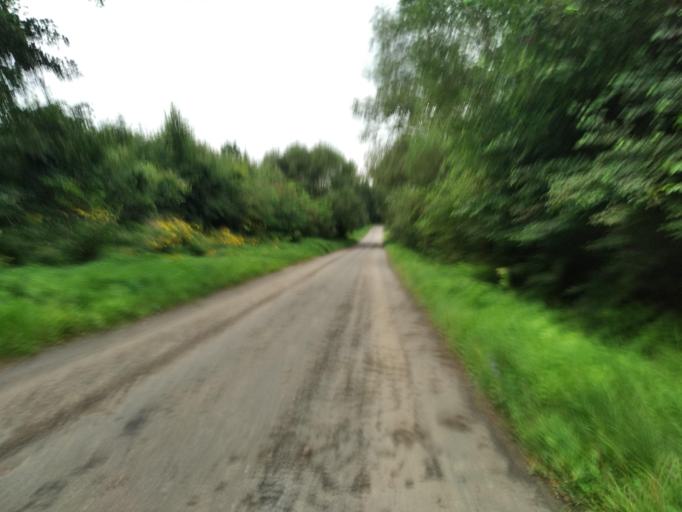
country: PL
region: Subcarpathian Voivodeship
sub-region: Powiat brzozowski
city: Dydnia
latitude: 49.6785
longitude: 22.2869
